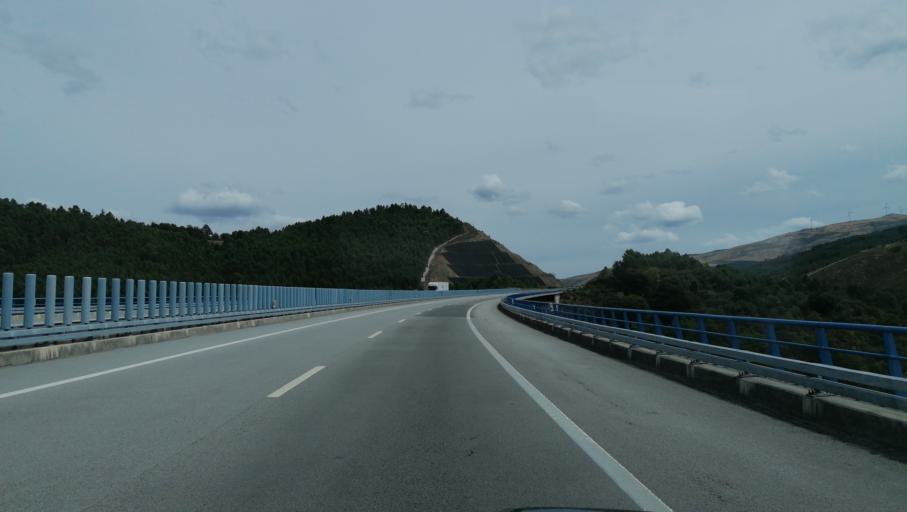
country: PT
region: Vila Real
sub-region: Ribeira de Pena
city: Ribeira de Pena
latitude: 41.4917
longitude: -7.8360
